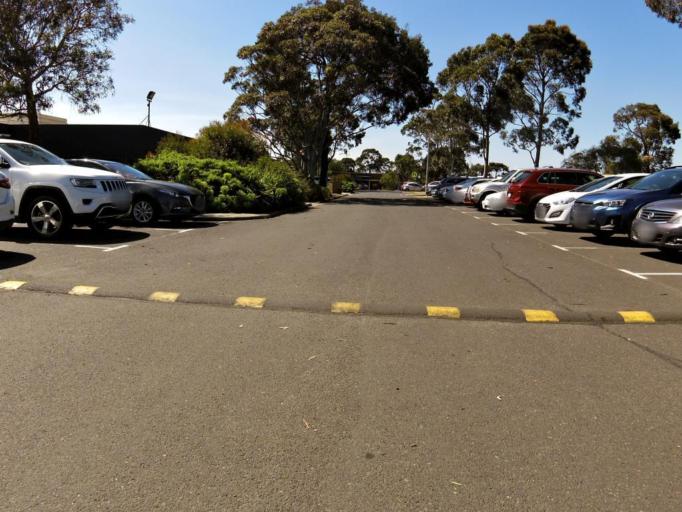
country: AU
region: Victoria
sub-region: Whitehorse
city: Blackburn South
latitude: -37.8489
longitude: 145.1623
